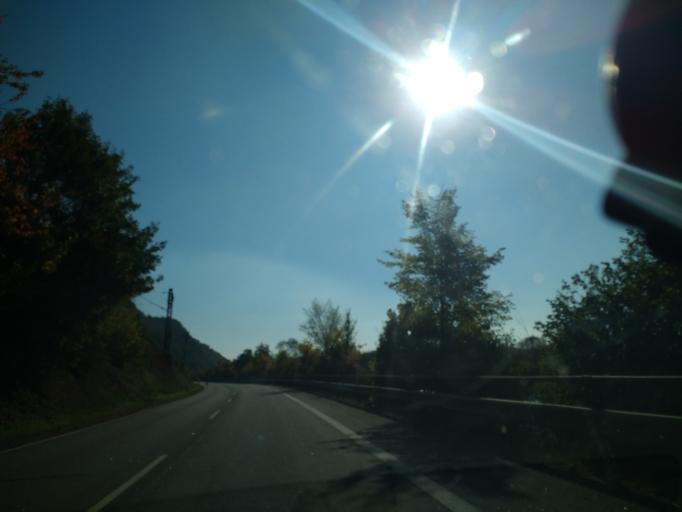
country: DE
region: Rheinland-Pfalz
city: Konz
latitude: 49.6890
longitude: 6.5669
